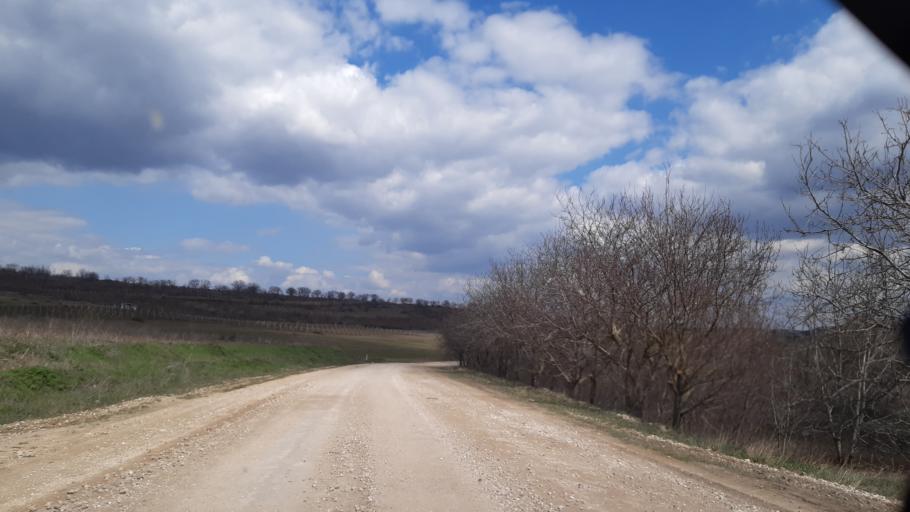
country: MD
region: Laloveni
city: Ialoveni
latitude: 46.8892
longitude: 28.7010
